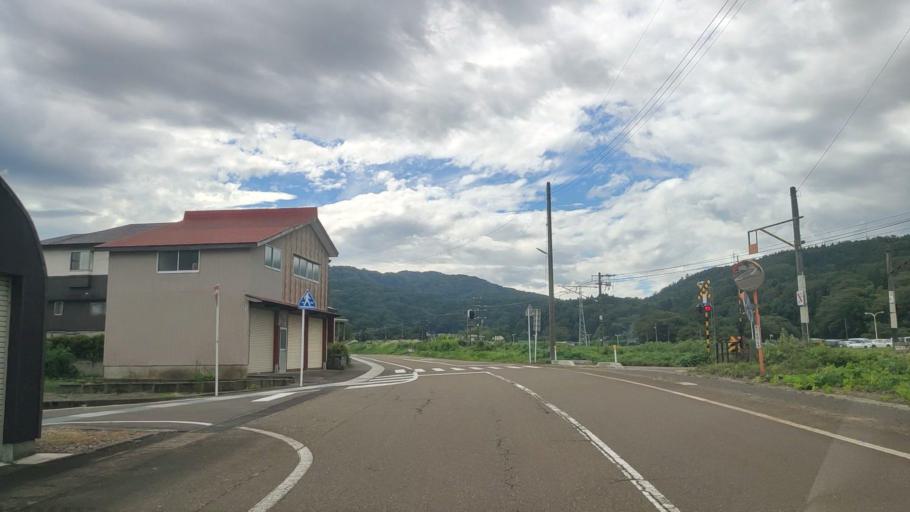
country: JP
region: Niigata
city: Arai
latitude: 37.0069
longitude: 138.2577
